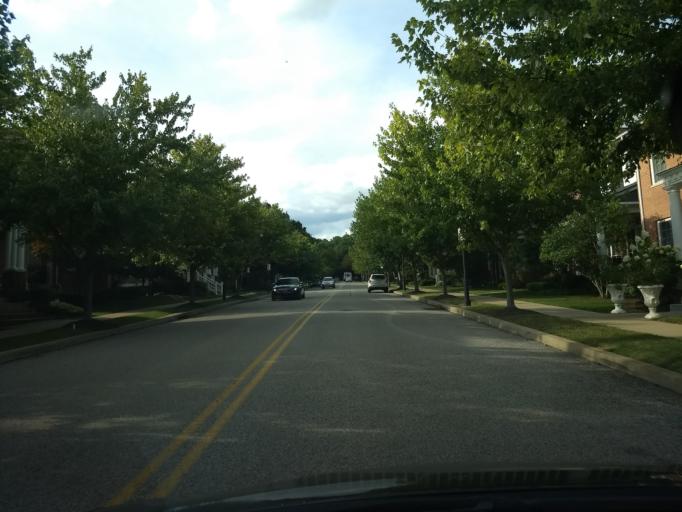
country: US
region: Pennsylvania
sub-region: Allegheny County
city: Homestead
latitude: 40.4234
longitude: -79.9118
